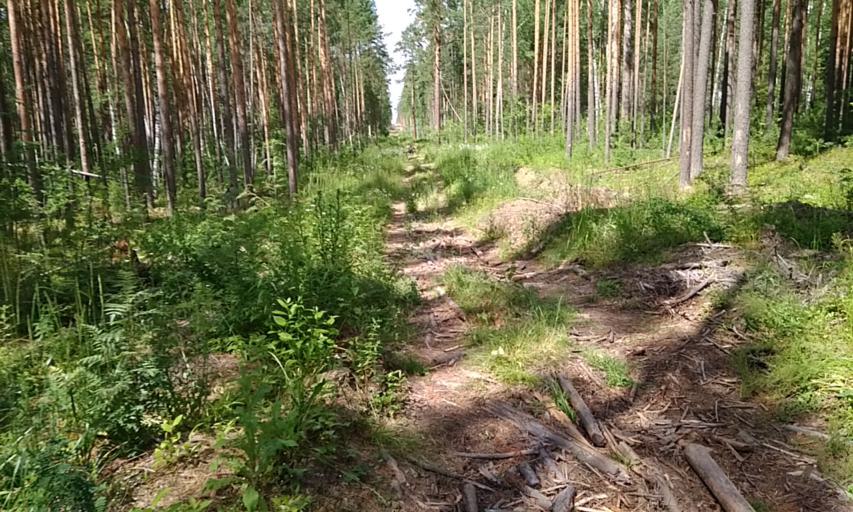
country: RU
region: Tomsk
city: Timiryazevskoye
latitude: 56.4065
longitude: 84.6639
